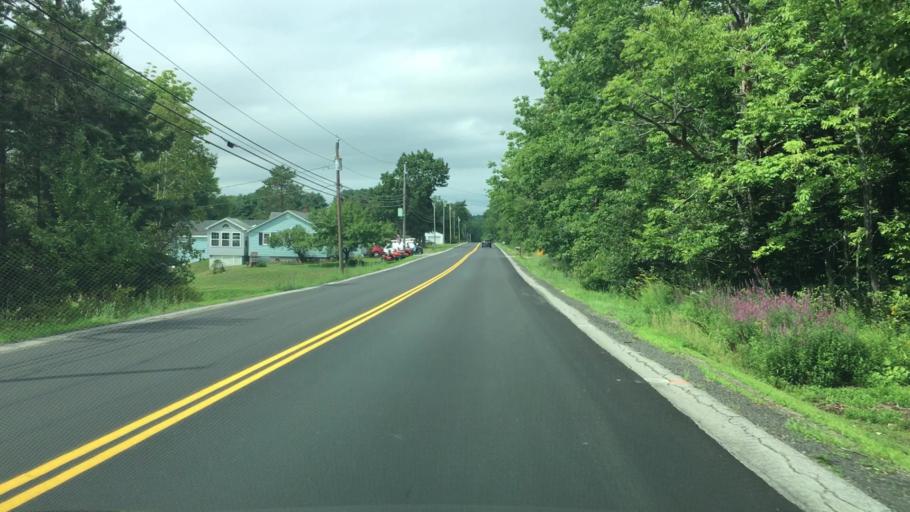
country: US
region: Maine
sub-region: Hancock County
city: Bucksport
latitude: 44.6063
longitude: -68.8192
